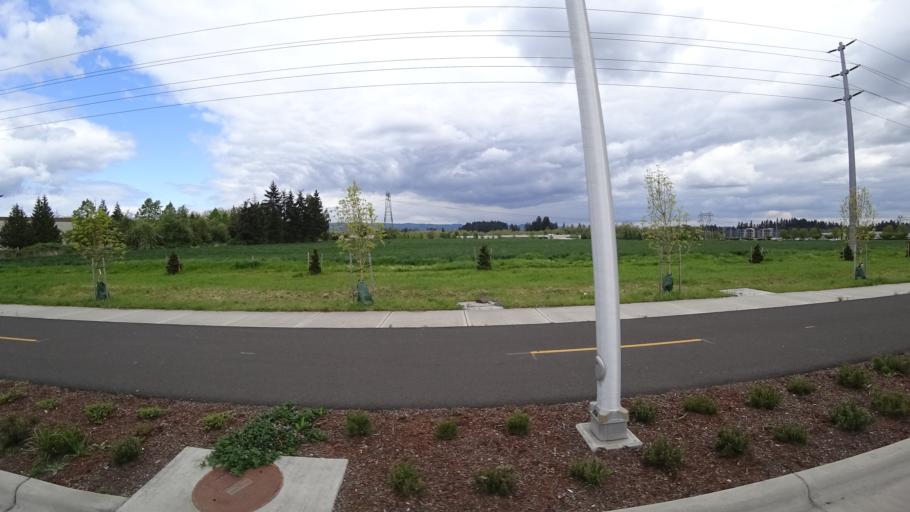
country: US
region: Oregon
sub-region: Washington County
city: Rockcreek
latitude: 45.5427
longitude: -122.8999
